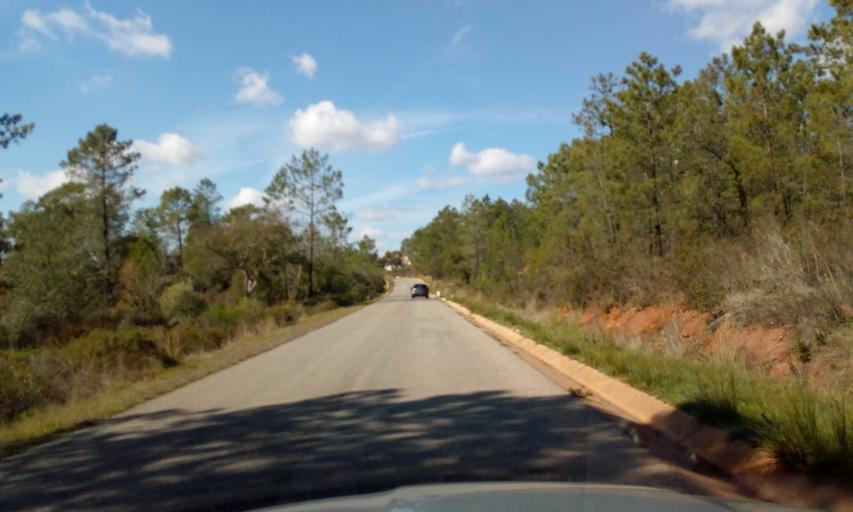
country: PT
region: Faro
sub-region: Loule
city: Loule
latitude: 37.2460
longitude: -8.0750
